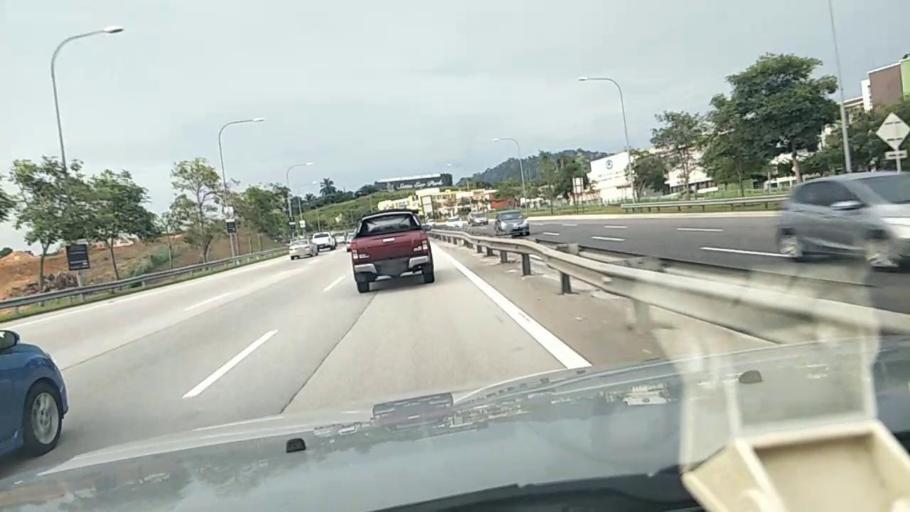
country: MY
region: Selangor
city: Shah Alam
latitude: 3.0953
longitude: 101.4824
